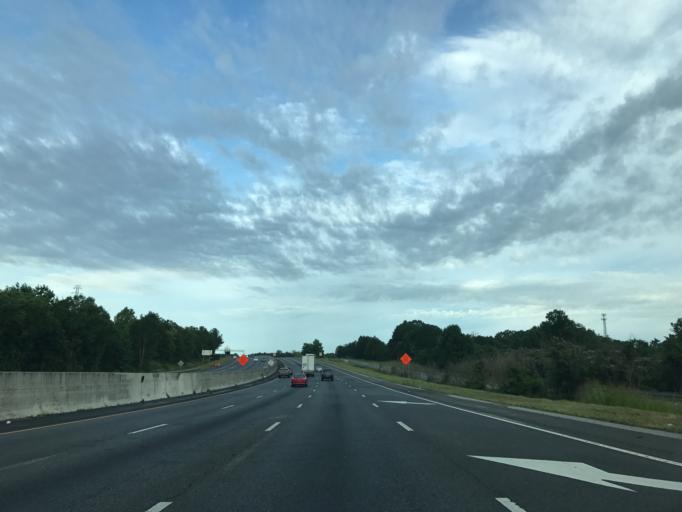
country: US
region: South Carolina
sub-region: Spartanburg County
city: Fairforest
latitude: 34.9633
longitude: -82.0449
